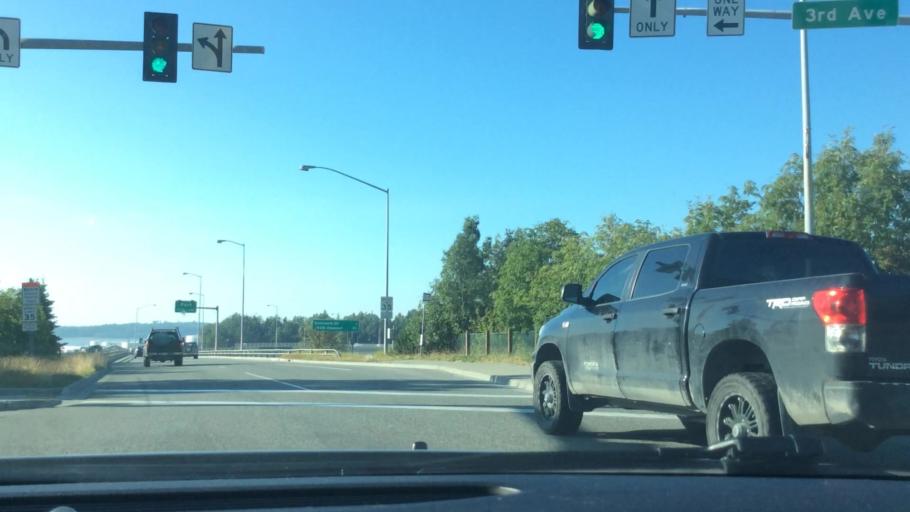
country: US
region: Alaska
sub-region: Anchorage Municipality
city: Anchorage
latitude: 61.2195
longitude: -149.8835
